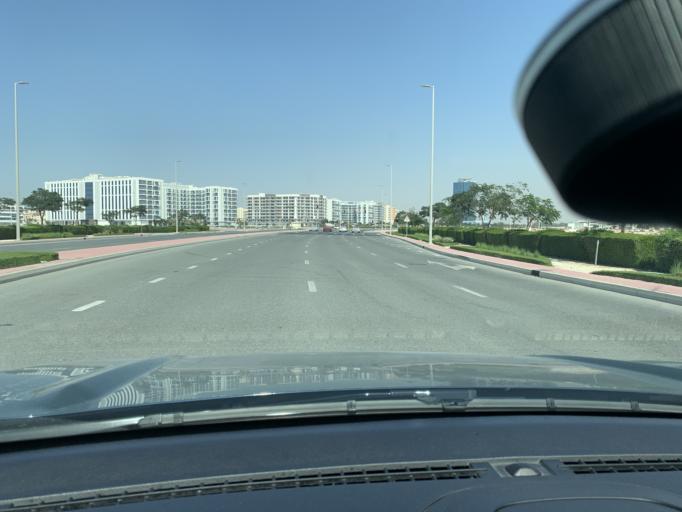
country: AE
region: Dubai
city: Dubai
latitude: 25.0364
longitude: 55.2440
